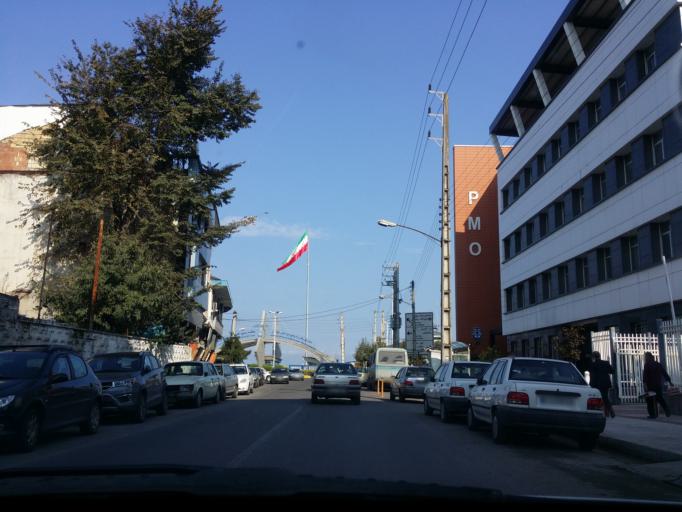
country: IR
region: Mazandaran
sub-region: Nowshahr
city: Nowshahr
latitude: 36.6513
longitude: 51.5087
